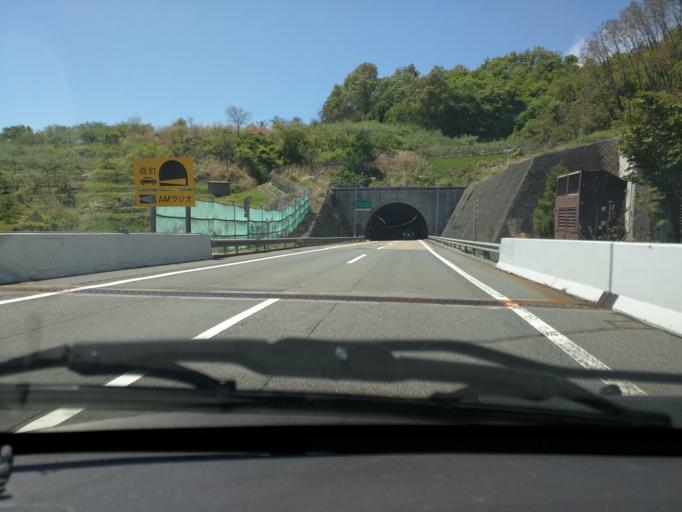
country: JP
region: Nagano
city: Nakano
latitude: 36.7540
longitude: 138.3131
